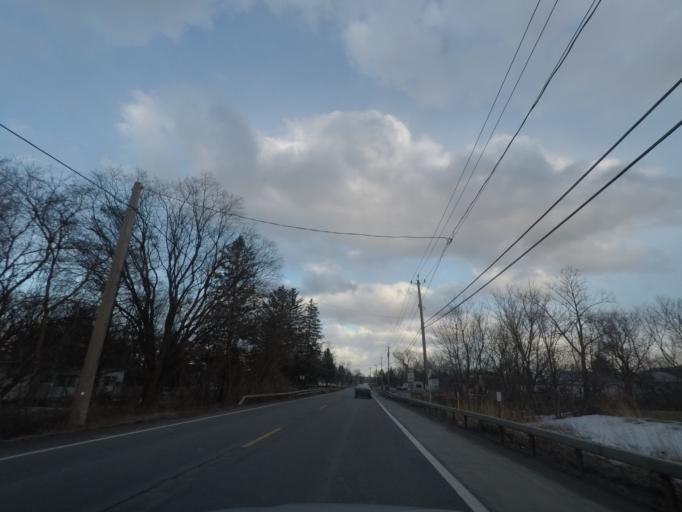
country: US
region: New York
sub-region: Herkimer County
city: Frankfort
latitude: 43.0943
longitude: -75.1412
